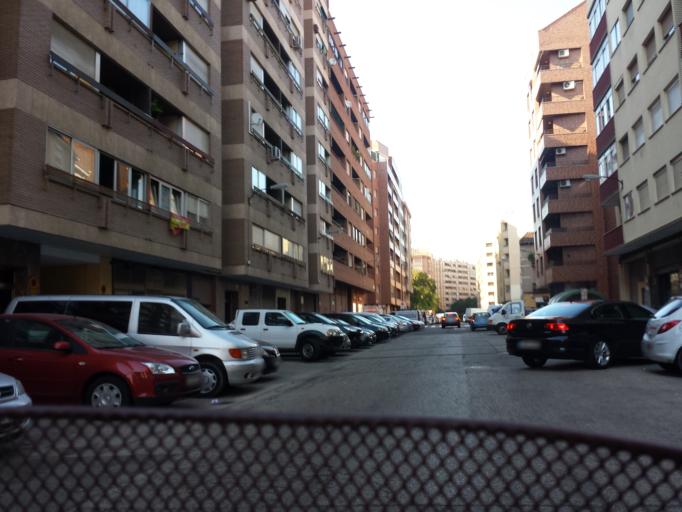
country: ES
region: Aragon
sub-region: Provincia de Zaragoza
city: Zaragoza
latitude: 41.6414
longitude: -0.8722
